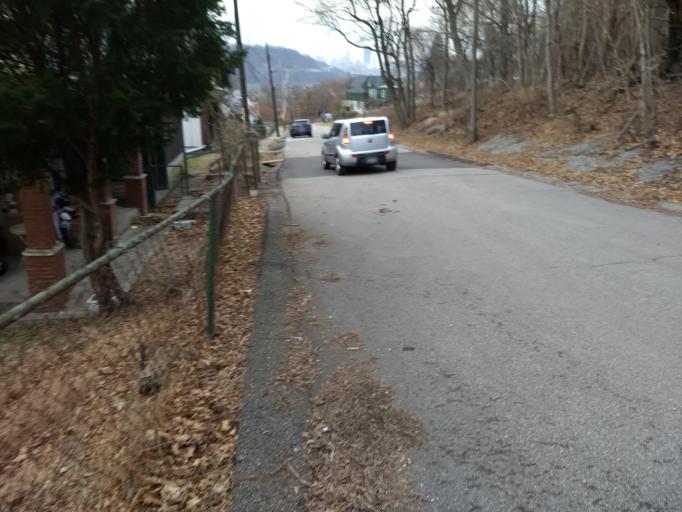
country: US
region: Pennsylvania
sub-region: Allegheny County
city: Homestead
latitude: 40.4073
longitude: -79.9367
